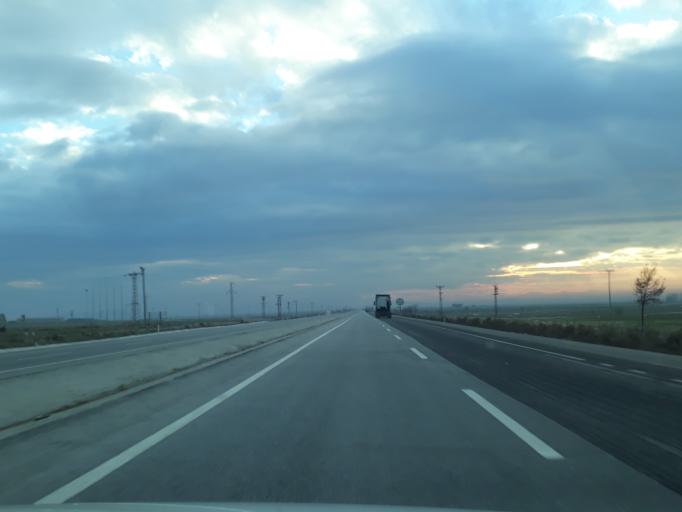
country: TR
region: Konya
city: Hotamis
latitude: 37.7107
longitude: 33.2795
